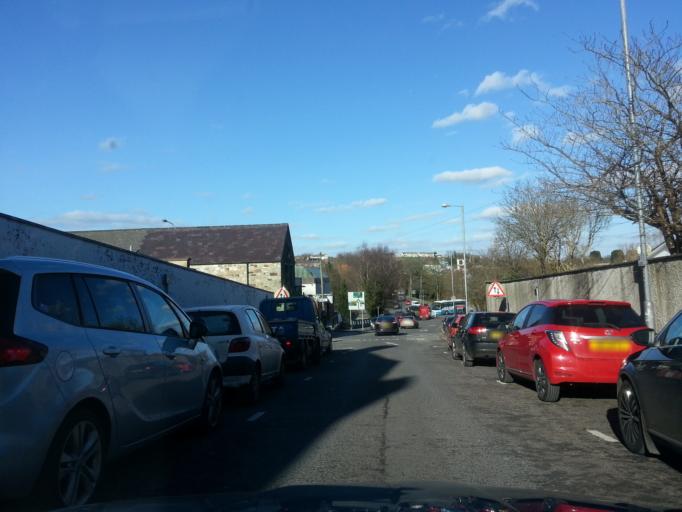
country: GB
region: Northern Ireland
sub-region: Fermanagh District
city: Enniskillen
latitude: 54.3466
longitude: -7.6413
